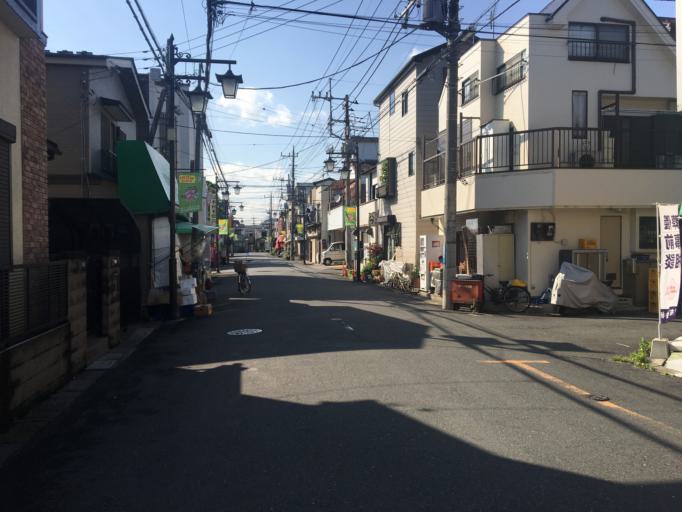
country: JP
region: Saitama
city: Shiki
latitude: 35.8476
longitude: 139.5637
